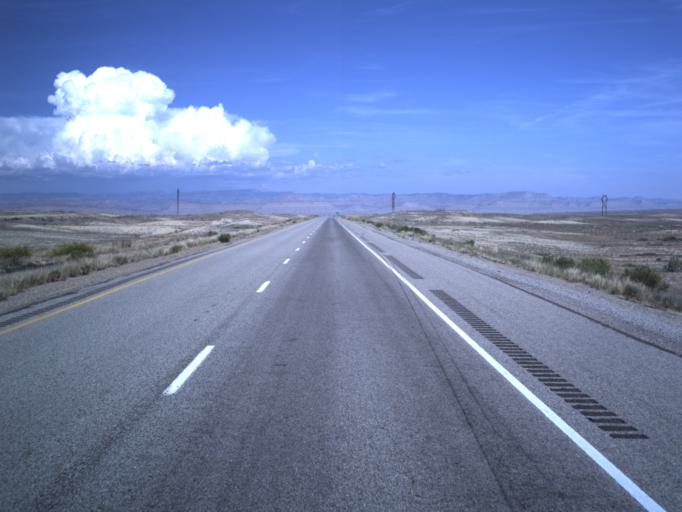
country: US
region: Utah
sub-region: Carbon County
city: East Carbon City
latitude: 38.9631
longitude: -110.2824
